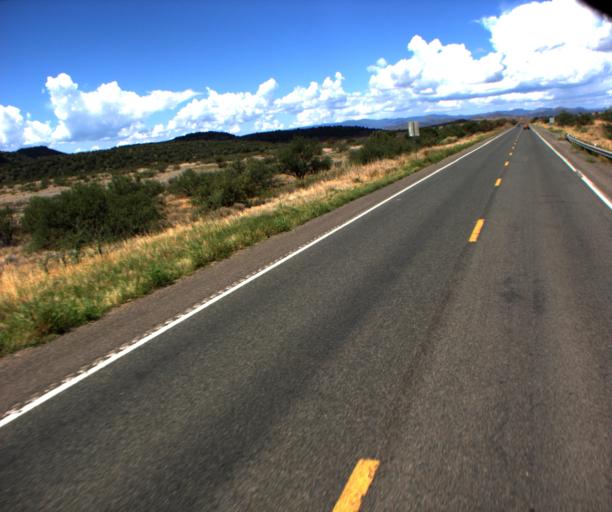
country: US
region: Arizona
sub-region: Yavapai County
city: Camp Verde
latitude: 34.5147
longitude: -112.0029
